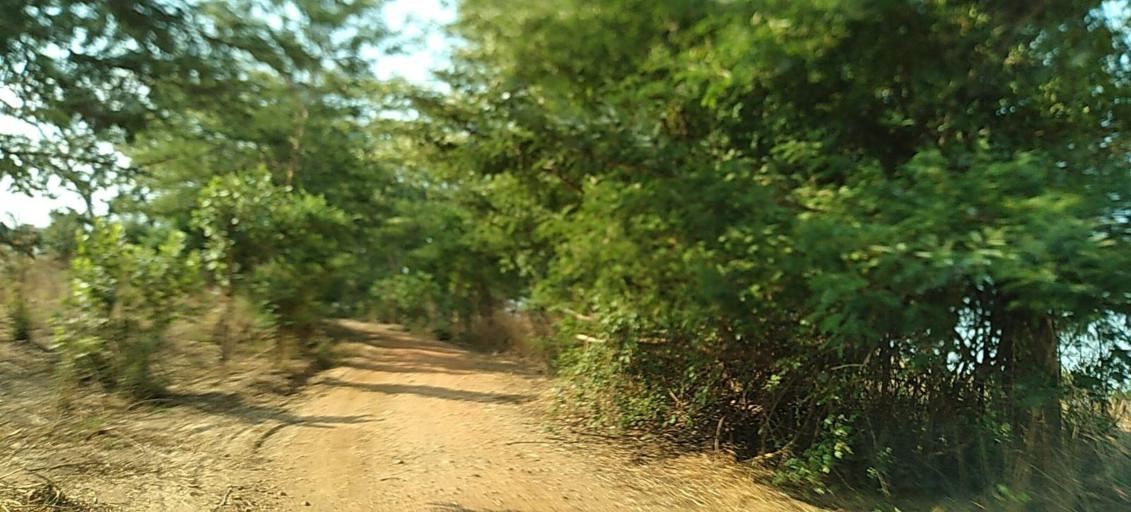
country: ZM
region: Copperbelt
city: Mpongwe
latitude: -13.4956
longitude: 28.0871
